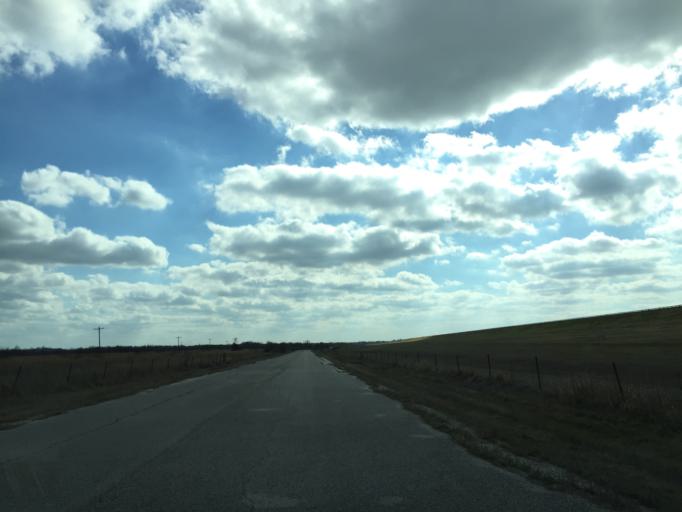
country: US
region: Texas
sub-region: Williamson County
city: Granger
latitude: 30.7112
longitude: -97.3234
